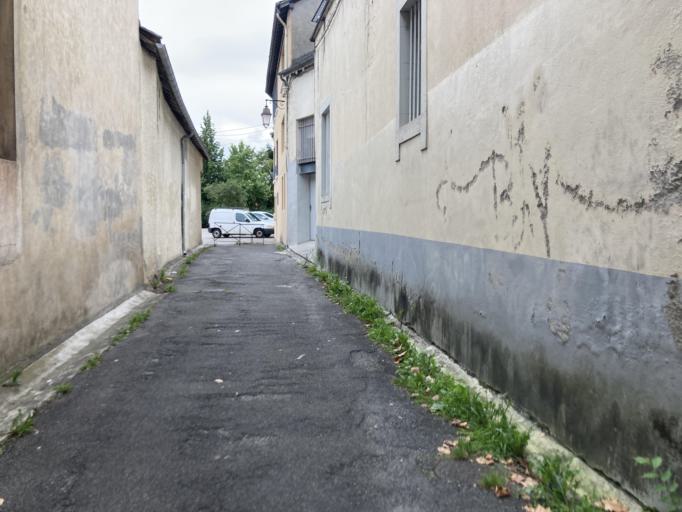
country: FR
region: Aquitaine
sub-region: Departement des Pyrenees-Atlantiques
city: Oloron-Sainte-Marie
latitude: 43.1917
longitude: -0.6095
